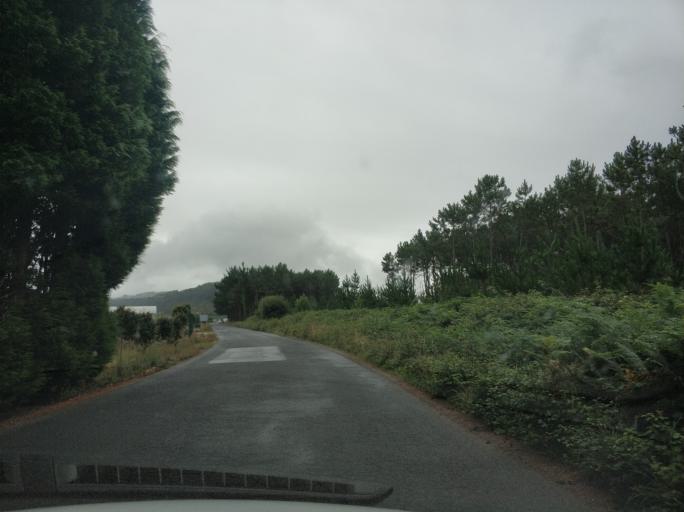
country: ES
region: Asturias
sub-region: Province of Asturias
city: Tineo
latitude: 43.5518
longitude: -6.4539
